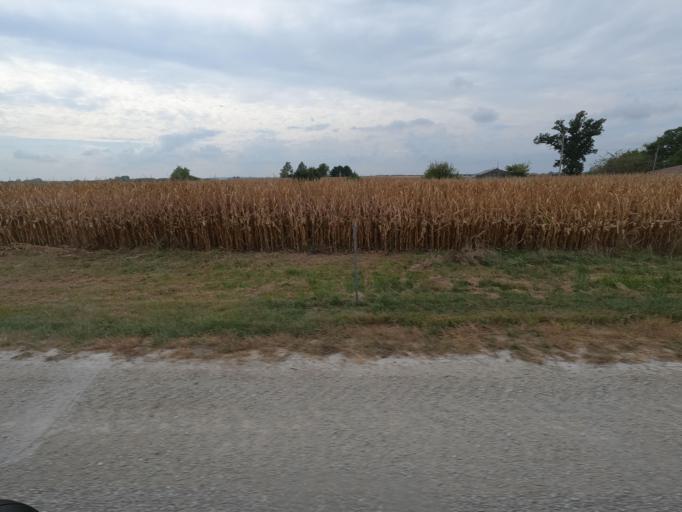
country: US
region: Iowa
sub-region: Jasper County
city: Monroe
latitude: 41.4703
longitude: -93.0411
